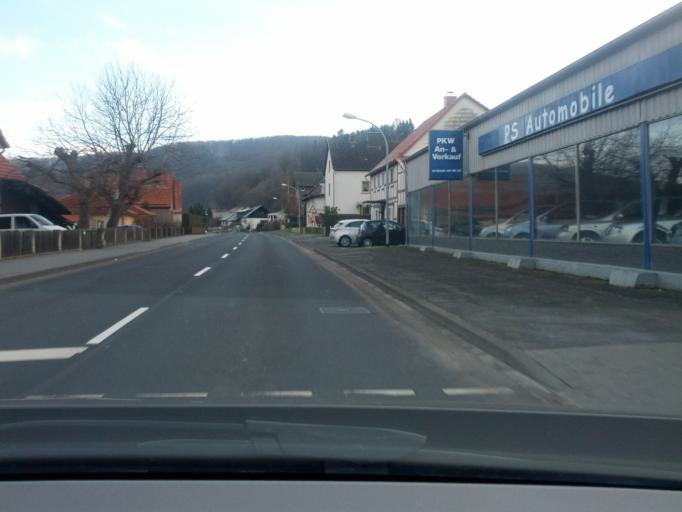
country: DE
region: Hesse
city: Witzenhausen
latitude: 51.3197
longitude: 9.8828
